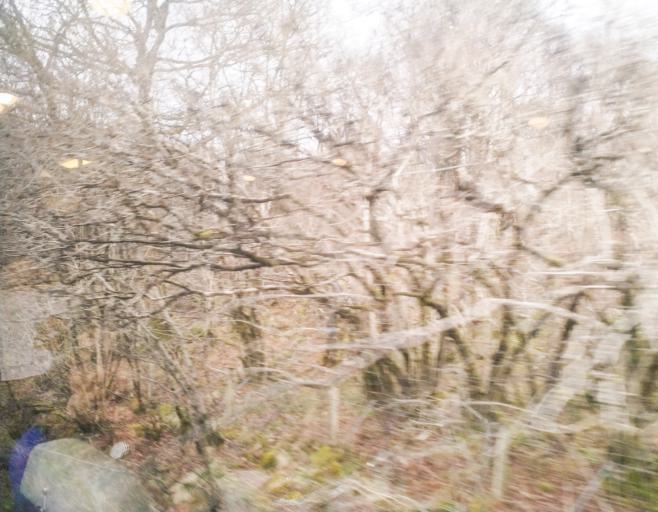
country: GB
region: Scotland
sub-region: Highland
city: Spean Bridge
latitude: 56.8923
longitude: -4.8829
